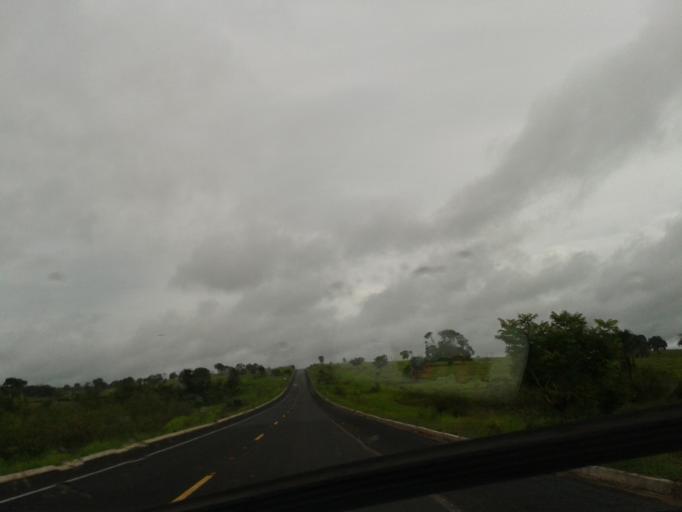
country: BR
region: Minas Gerais
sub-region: Santa Vitoria
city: Santa Vitoria
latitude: -19.2666
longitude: -50.0065
